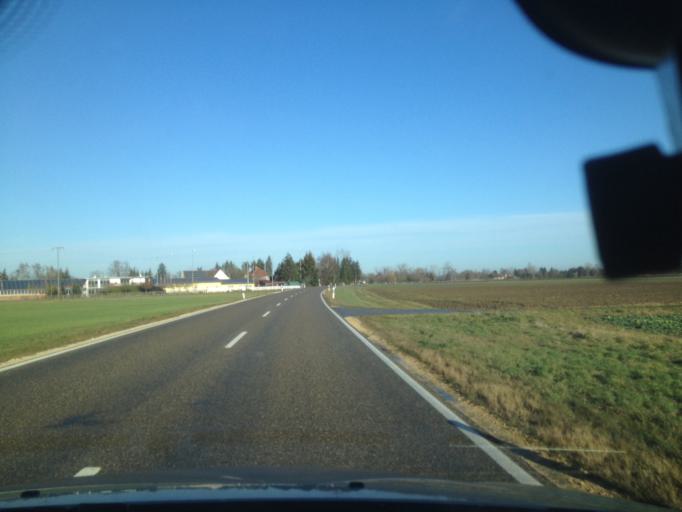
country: DE
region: Bavaria
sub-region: Swabia
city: Offingen
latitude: 48.5015
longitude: 10.3613
